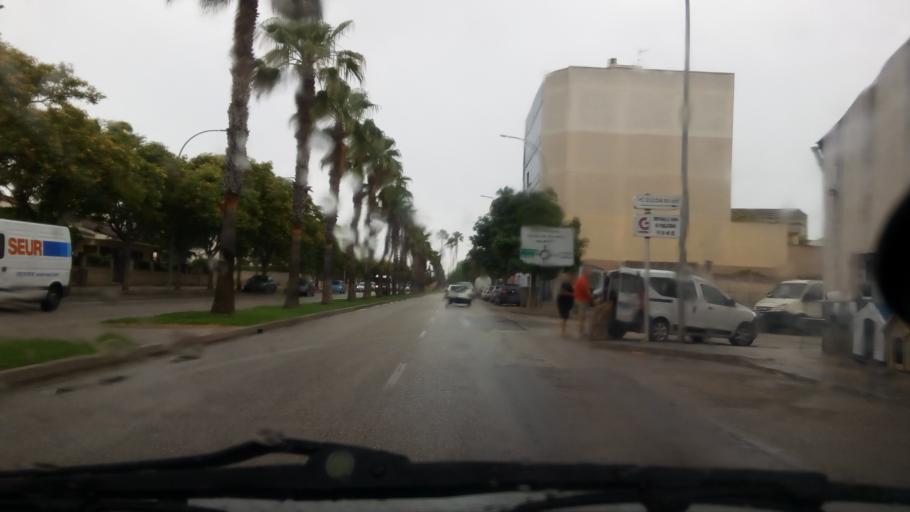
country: ES
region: Balearic Islands
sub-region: Illes Balears
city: Manacor
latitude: 39.5717
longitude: 3.2180
